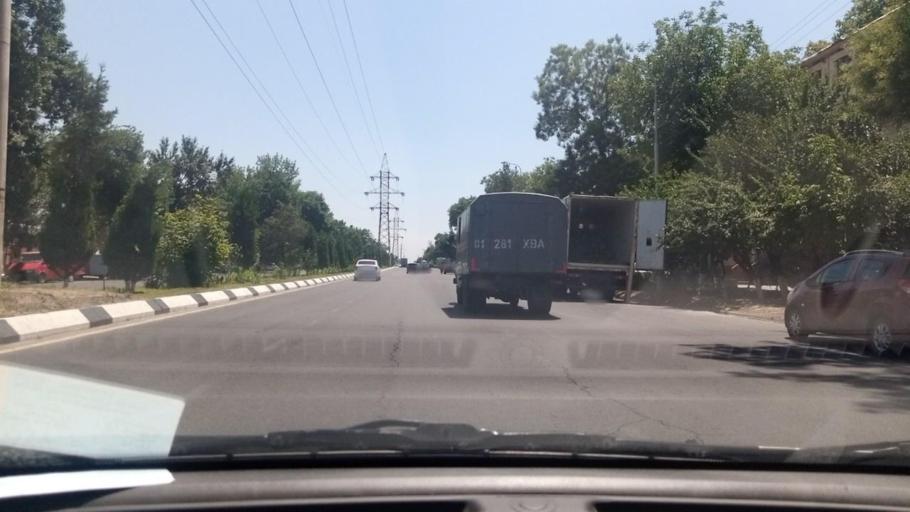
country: UZ
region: Toshkent Shahri
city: Tashkent
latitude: 41.2948
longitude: 69.1943
